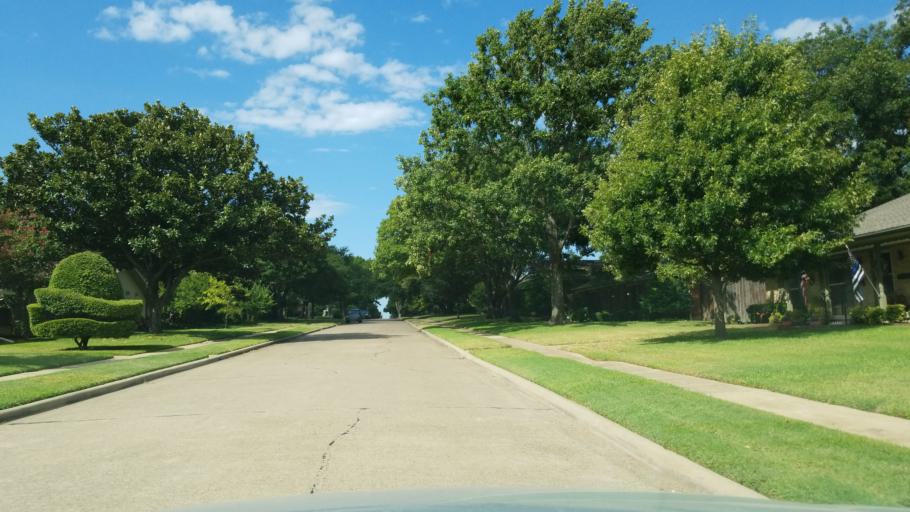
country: US
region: Texas
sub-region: Dallas County
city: Richardson
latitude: 32.9687
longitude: -96.7735
